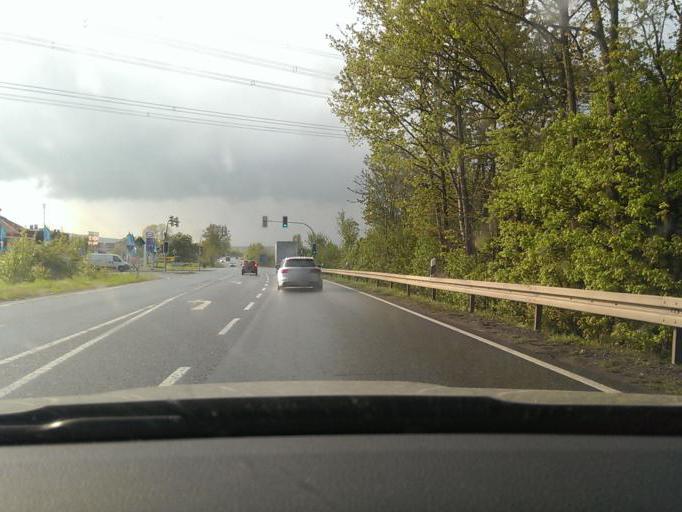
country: DE
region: Lower Saxony
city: Pohle
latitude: 52.2775
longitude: 9.3542
